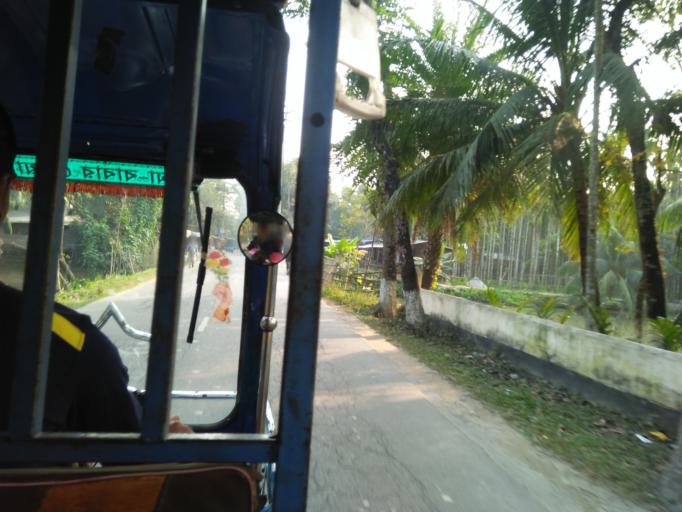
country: BD
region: Barisal
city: Bhola
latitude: 22.7079
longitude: 90.6400
